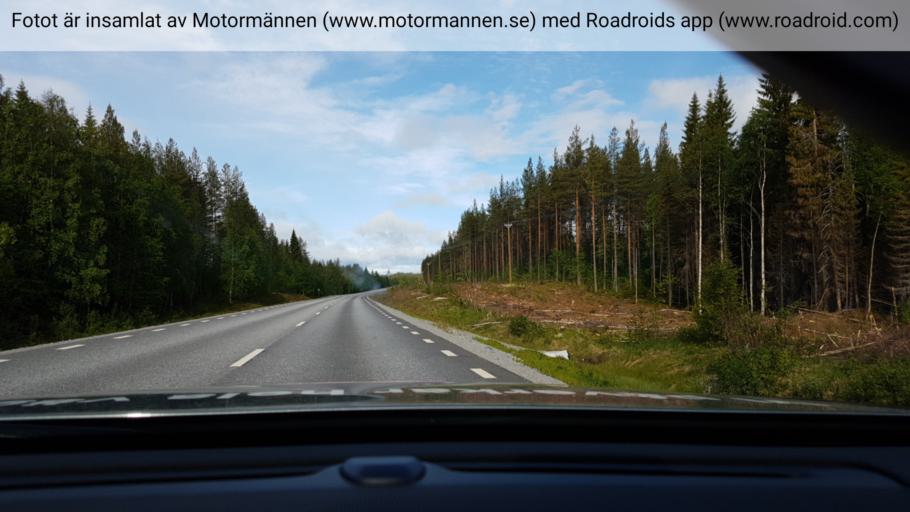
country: SE
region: Vaesterbotten
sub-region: Asele Kommun
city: Insjon
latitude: 64.1445
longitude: 17.9642
